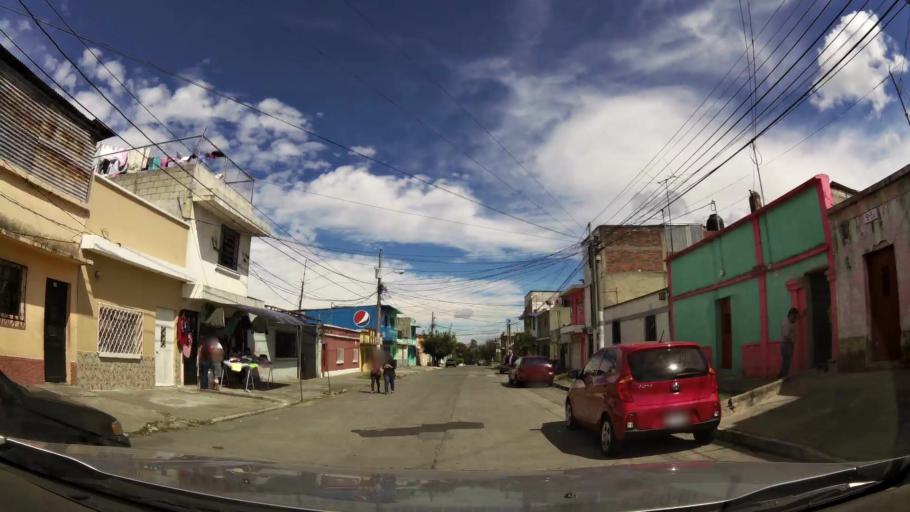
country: GT
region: Guatemala
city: Mixco
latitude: 14.6593
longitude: -90.5739
